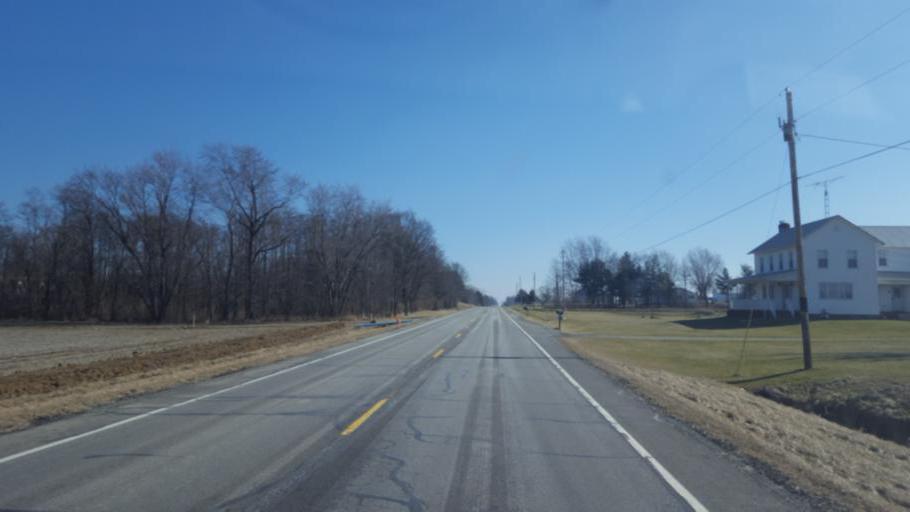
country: US
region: Ohio
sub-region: Huron County
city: Plymouth
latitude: 41.0314
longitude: -82.6266
